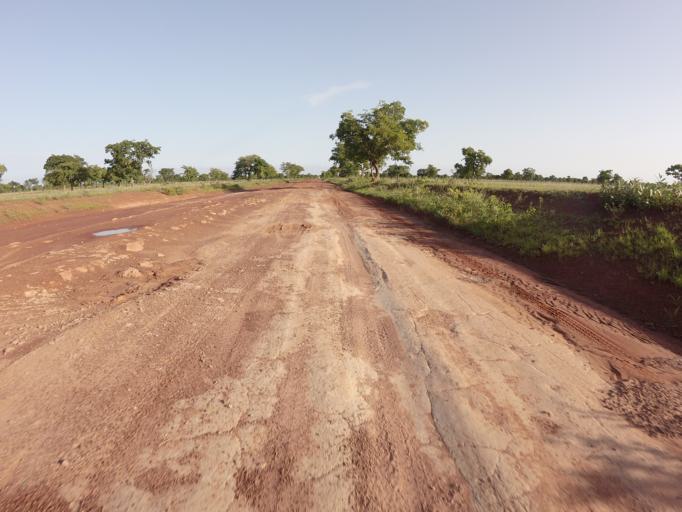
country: TG
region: Savanes
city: Sansanne-Mango
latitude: 10.3735
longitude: -0.0943
